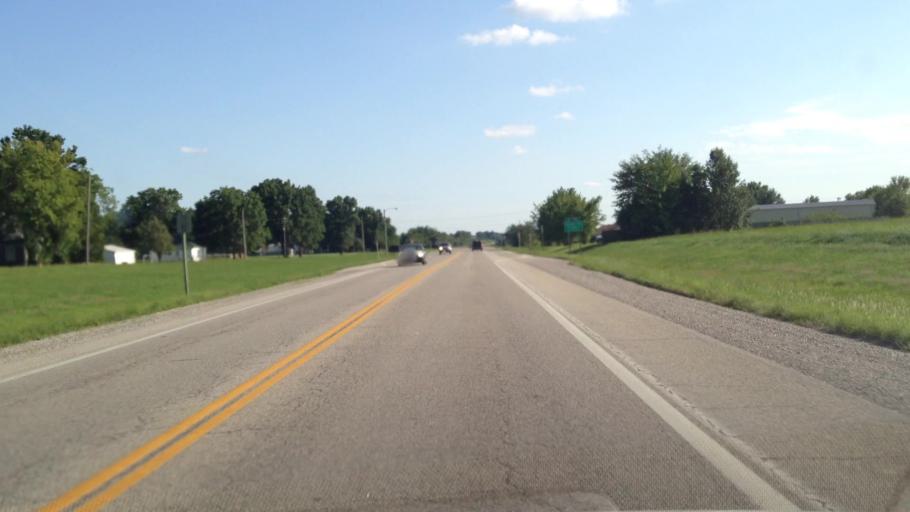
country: US
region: Kansas
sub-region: Crawford County
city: Arma
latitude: 37.5450
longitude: -94.7102
